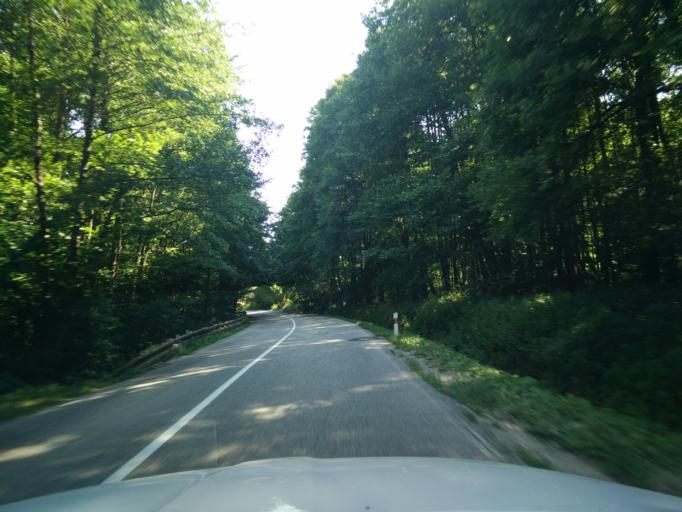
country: SK
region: Nitriansky
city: Bojnice
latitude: 48.8513
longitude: 18.4673
